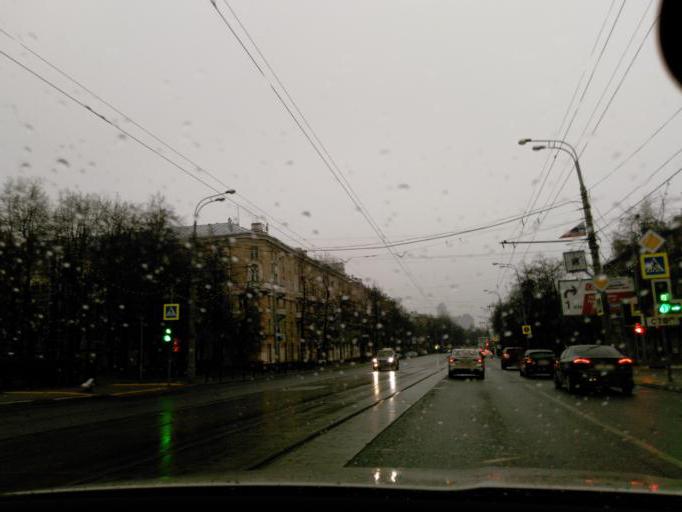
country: RU
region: Moscow
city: Pokrovskoye-Streshnevo
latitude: 55.8288
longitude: 37.4527
